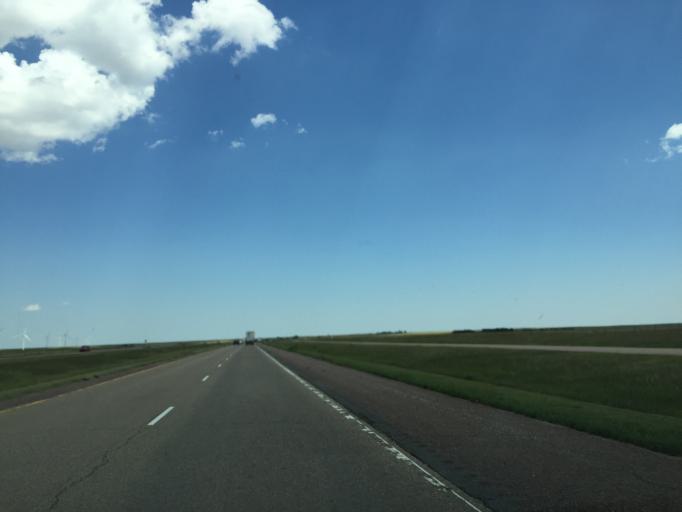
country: US
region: Colorado
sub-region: Lincoln County
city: Hugo
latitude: 39.2787
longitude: -103.4132
